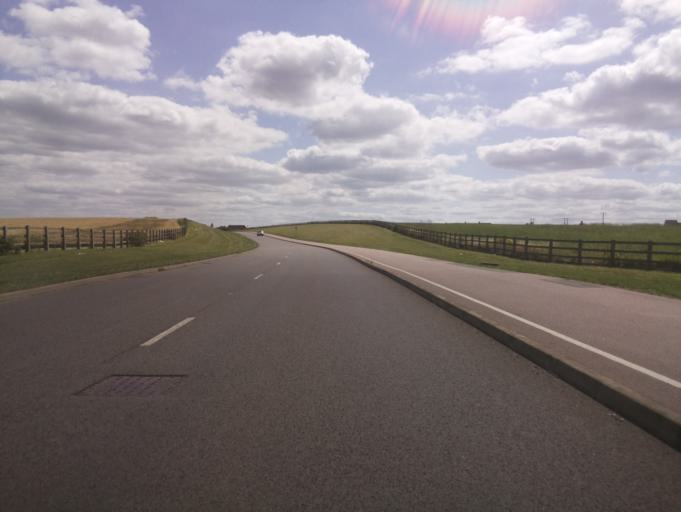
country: GB
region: England
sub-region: Buckinghamshire
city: Aylesbury
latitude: 51.8373
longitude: -0.8284
